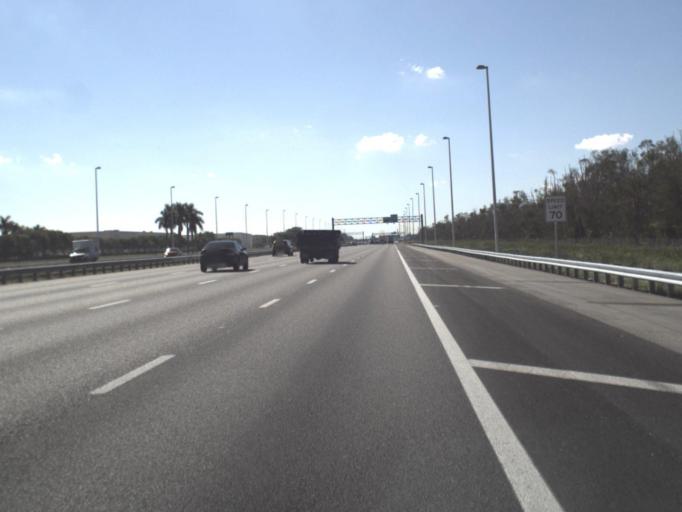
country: US
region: Florida
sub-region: Miami-Dade County
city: Doral
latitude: 25.8628
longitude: -80.3879
